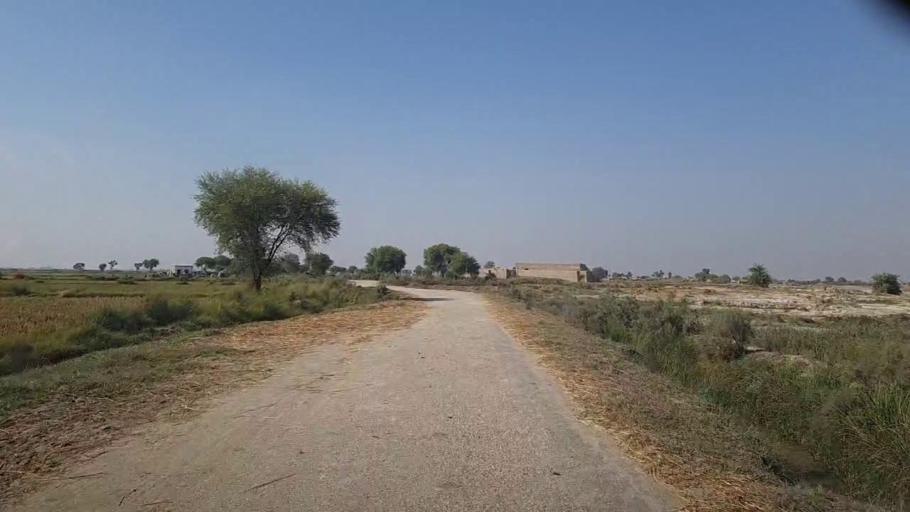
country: PK
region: Sindh
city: Tangwani
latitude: 28.2490
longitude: 68.9434
